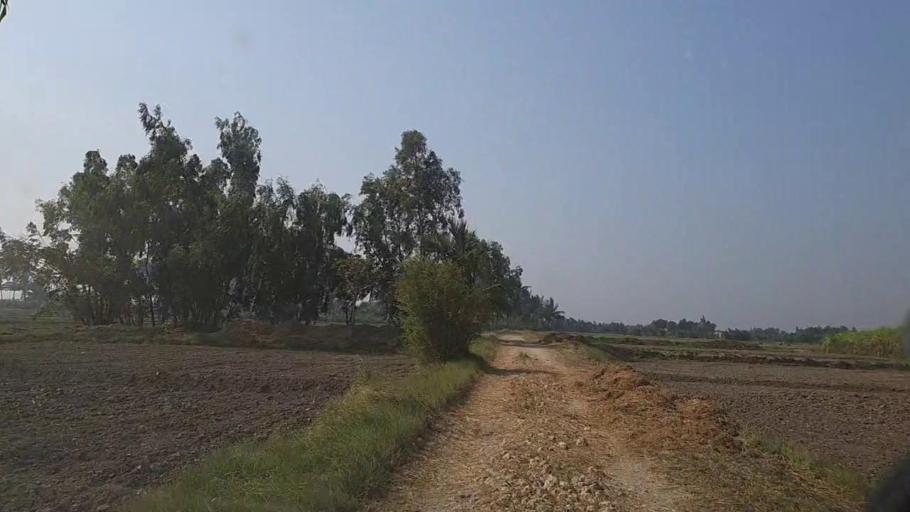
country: PK
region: Sindh
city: Thatta
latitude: 24.6555
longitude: 67.9185
